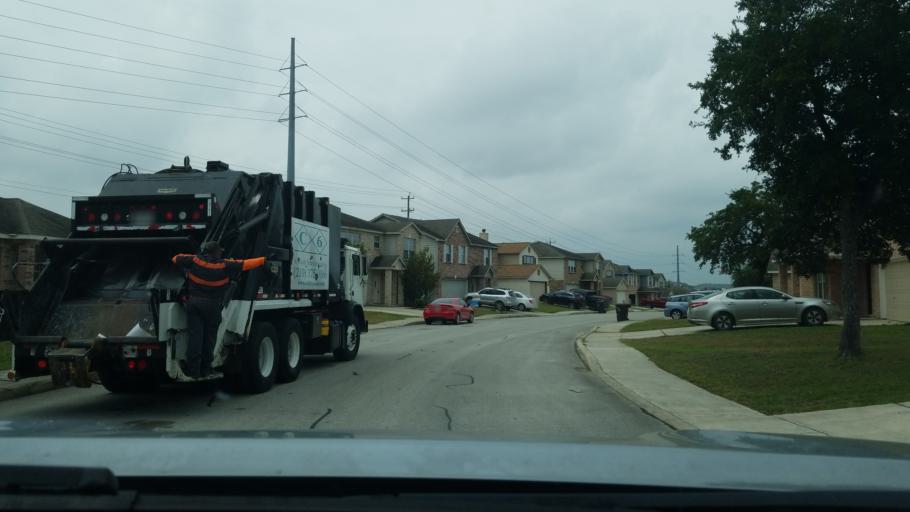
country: US
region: Texas
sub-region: Bexar County
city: Timberwood Park
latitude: 29.6803
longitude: -98.4665
